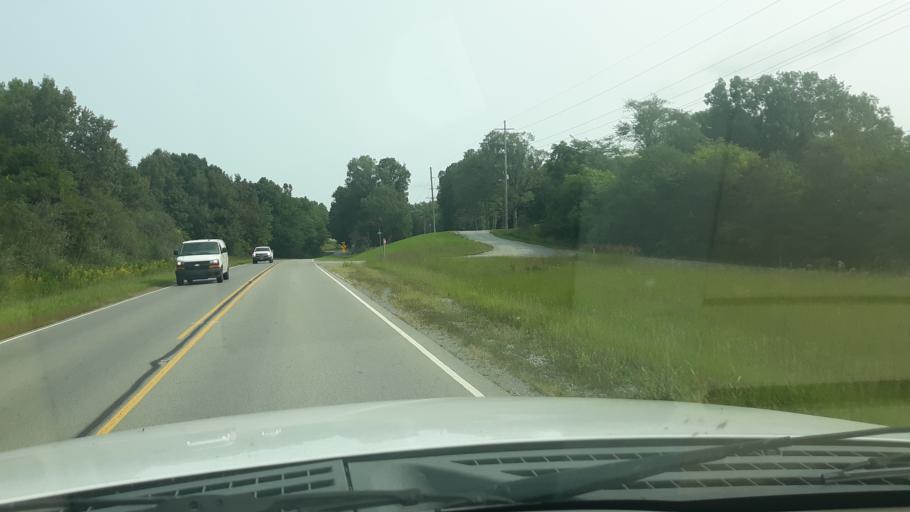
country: US
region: Illinois
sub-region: White County
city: Norris City
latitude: 37.9189
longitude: -88.3526
